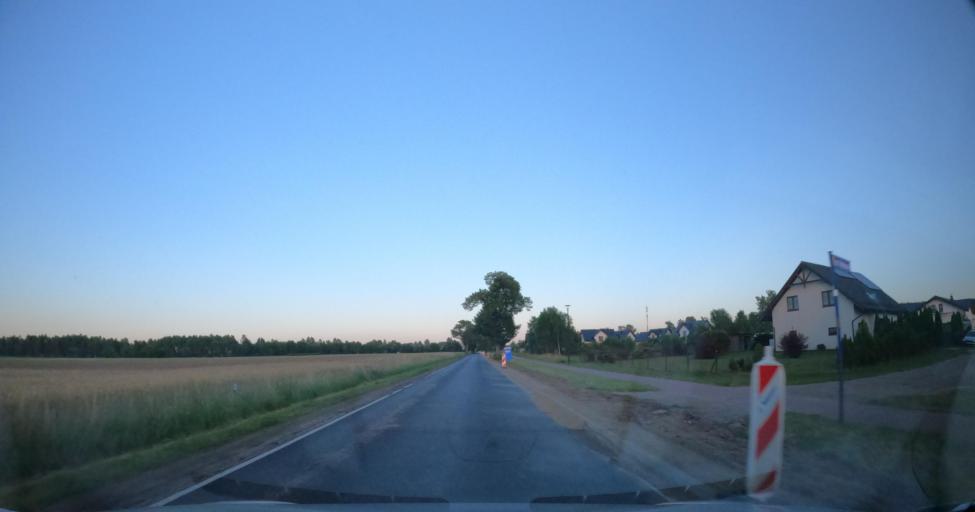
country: PL
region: Pomeranian Voivodeship
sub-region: Powiat wejherowski
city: Linia
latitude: 54.4540
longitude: 17.9184
